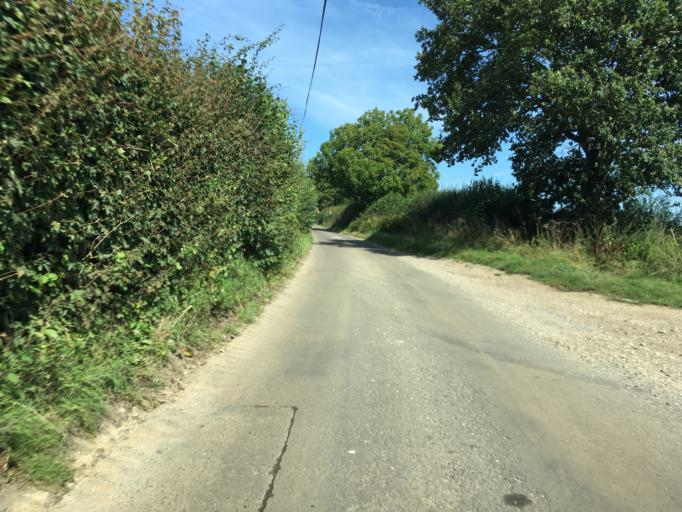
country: GB
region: England
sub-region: Hampshire
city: Highclere
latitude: 51.2971
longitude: -1.3797
